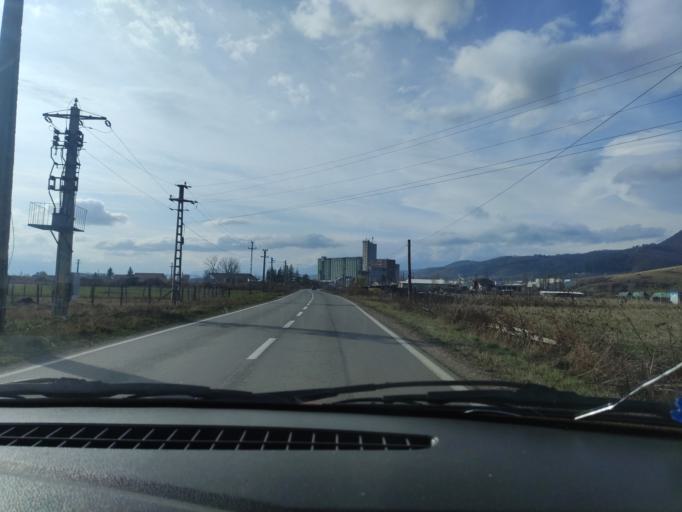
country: RO
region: Brasov
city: Codlea
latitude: 45.7120
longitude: 25.4643
